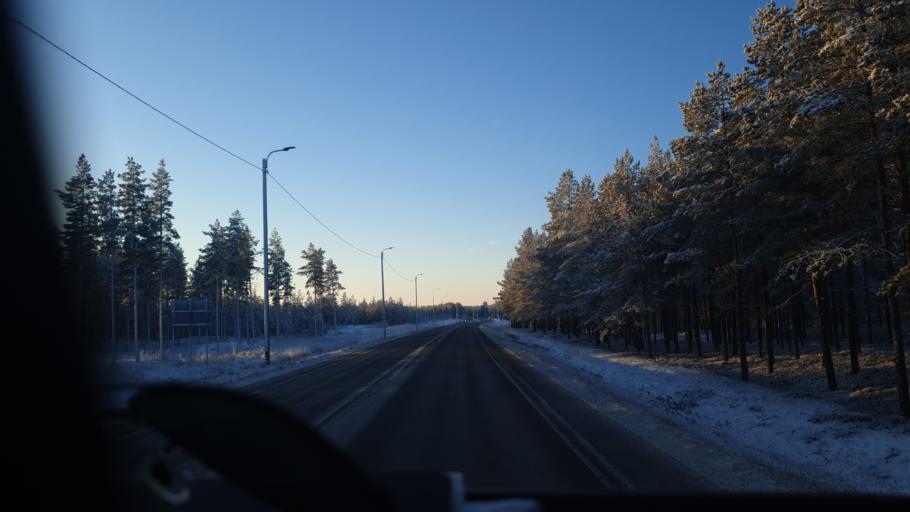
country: FI
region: Northern Ostrobothnia
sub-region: Ylivieska
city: Kalajoki
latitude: 64.2332
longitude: 23.8246
